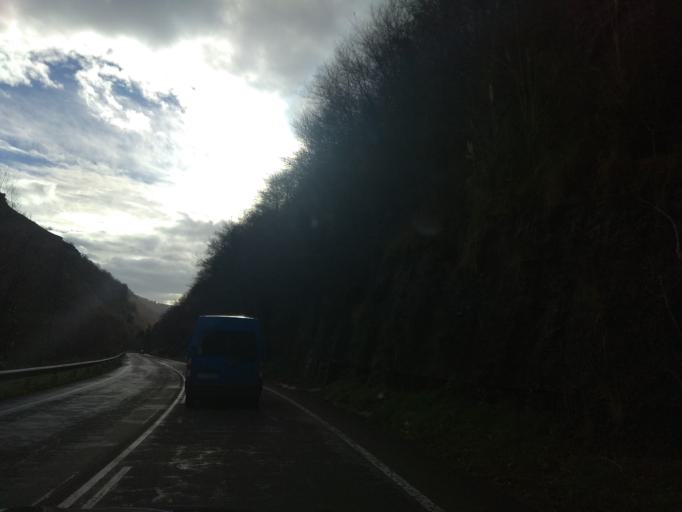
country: ES
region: Cantabria
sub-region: Provincia de Cantabria
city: San Pedro del Romeral
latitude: 43.1391
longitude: -3.9008
